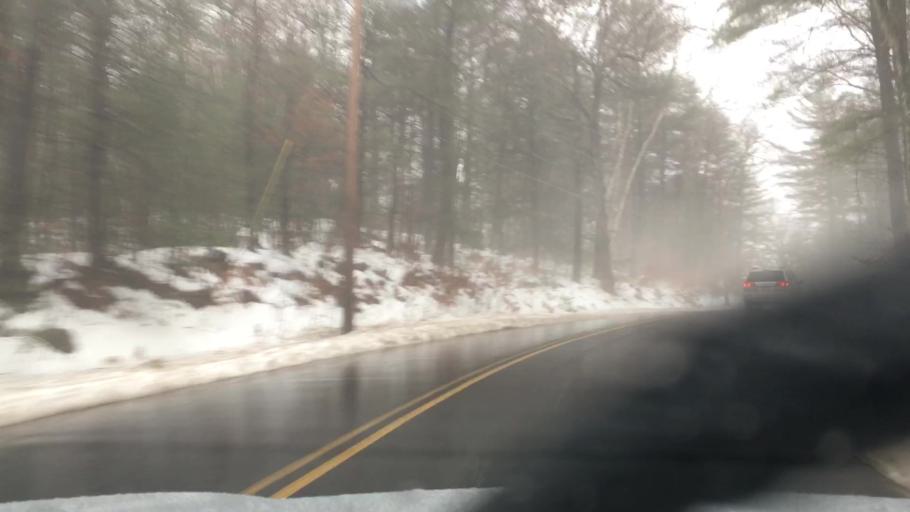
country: US
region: Massachusetts
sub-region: Hampshire County
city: Granby
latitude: 42.2497
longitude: -72.4734
